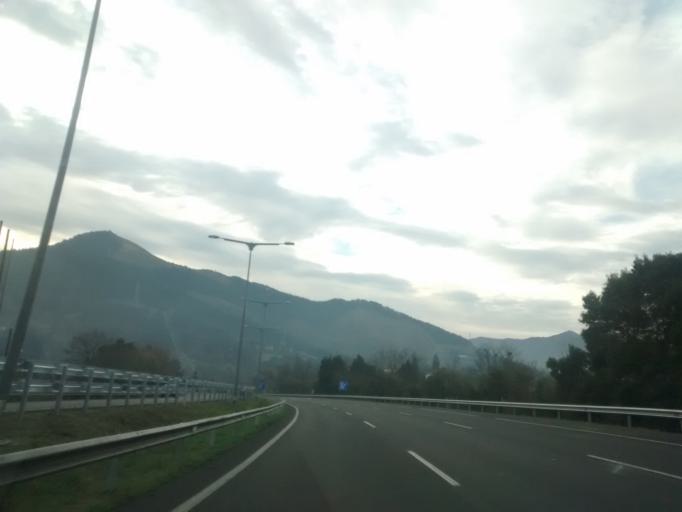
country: ES
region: Basque Country
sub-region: Bizkaia
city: Arrigorriaga
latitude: 43.2101
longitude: -2.8950
